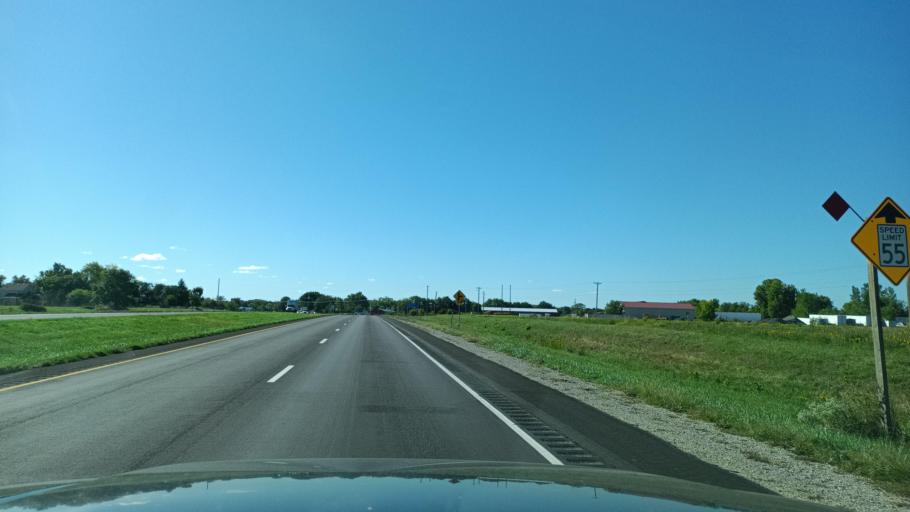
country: US
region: Iowa
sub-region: Lee County
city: Keokuk
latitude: 40.4508
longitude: -91.4425
